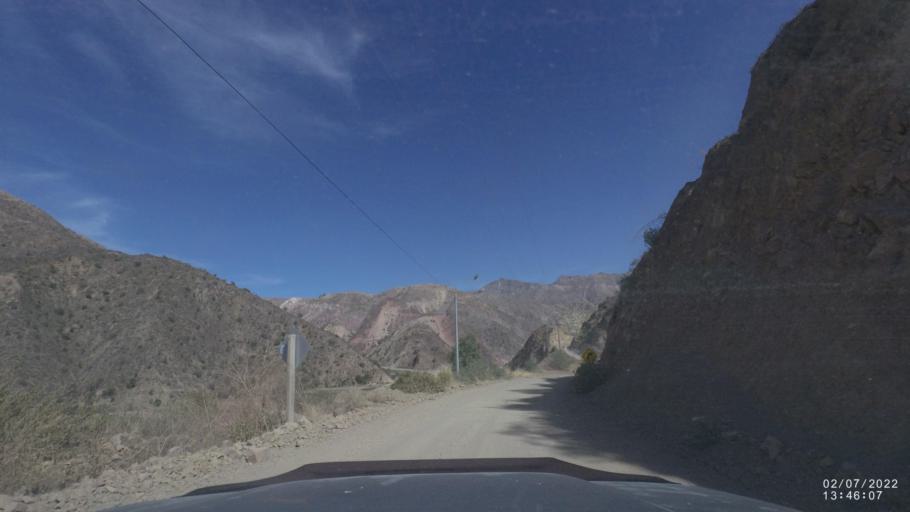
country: BO
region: Cochabamba
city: Irpa Irpa
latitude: -17.8121
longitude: -66.3655
